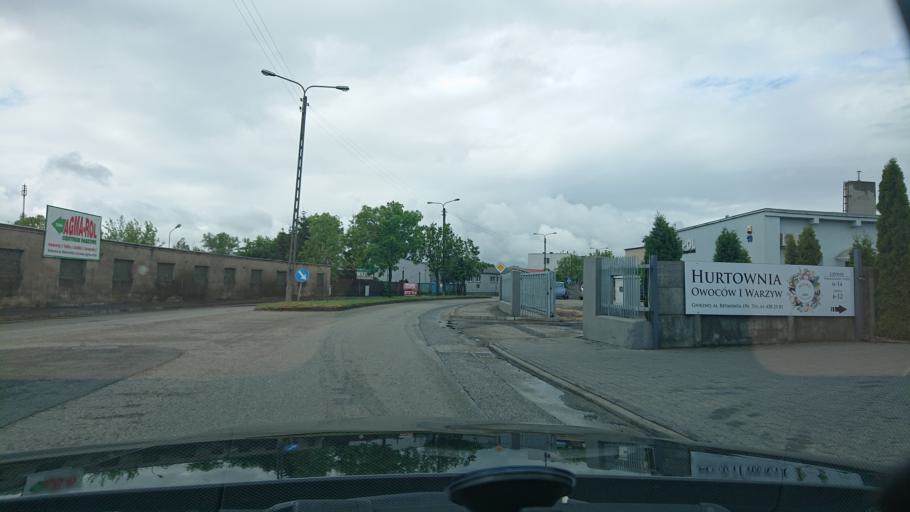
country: PL
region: Greater Poland Voivodeship
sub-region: Powiat gnieznienski
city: Gniezno
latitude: 52.5334
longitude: 17.6246
